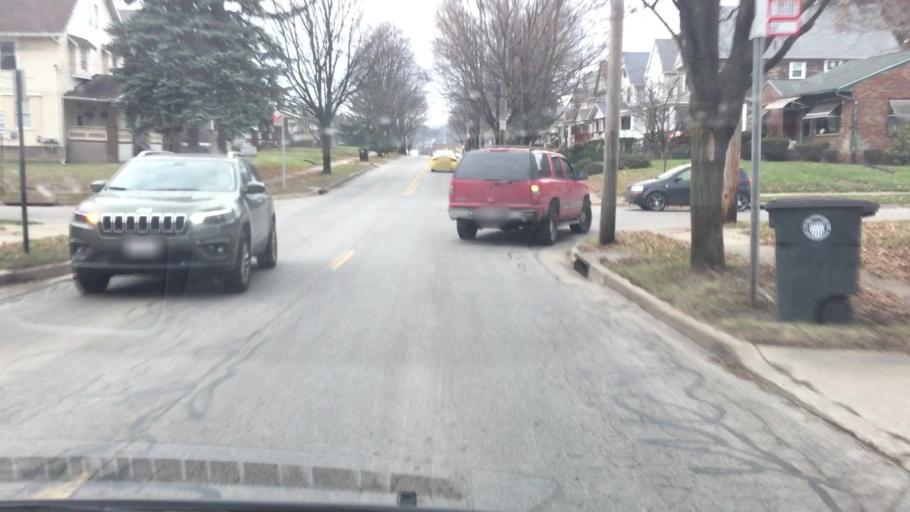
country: US
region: Ohio
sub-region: Summit County
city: Akron
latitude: 41.0467
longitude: -81.5248
